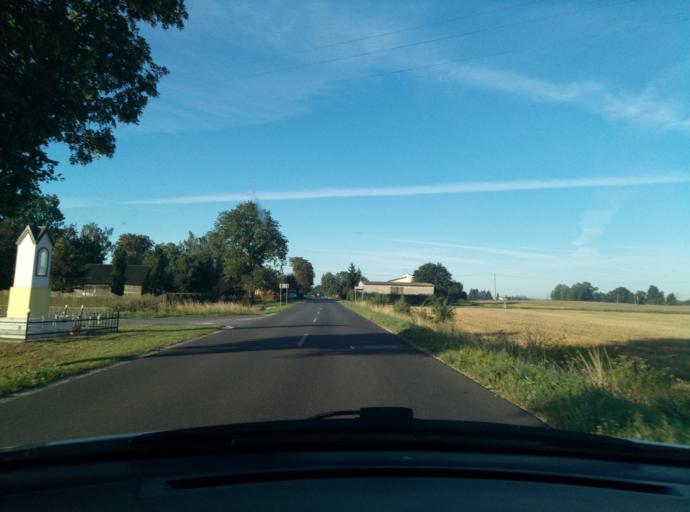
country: PL
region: Kujawsko-Pomorskie
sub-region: Powiat golubsko-dobrzynski
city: Kowalewo Pomorskie
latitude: 53.2050
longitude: 18.9194
